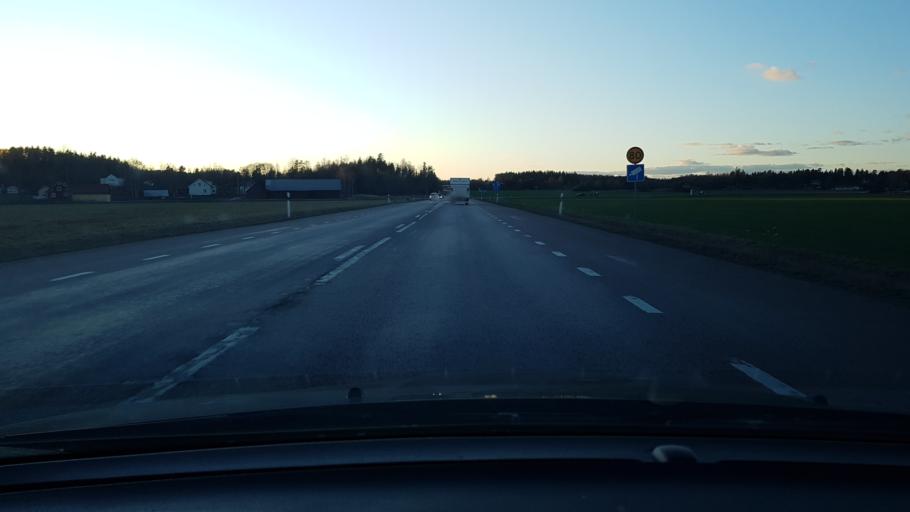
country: SE
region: Uppsala
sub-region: Knivsta Kommun
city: Knivsta
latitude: 59.7501
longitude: 17.9165
